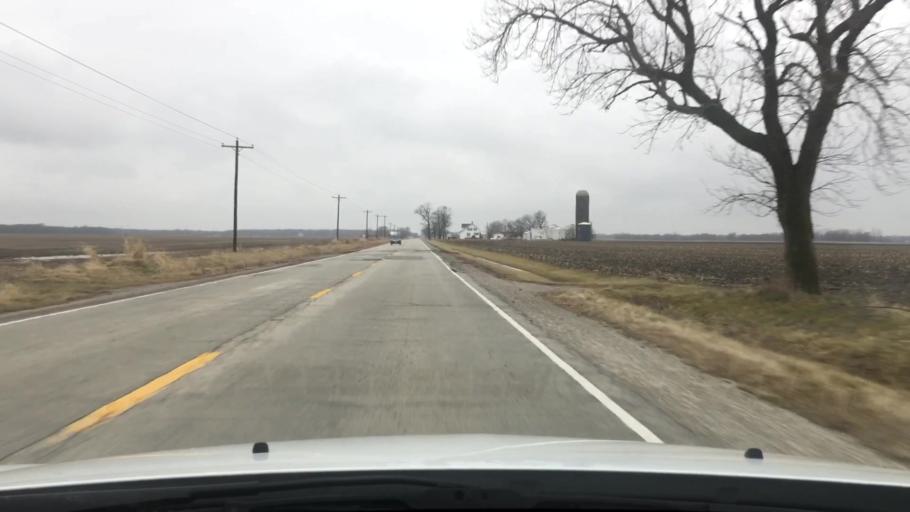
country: US
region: Illinois
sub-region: Iroquois County
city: Watseka
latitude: 40.8885
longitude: -87.7983
